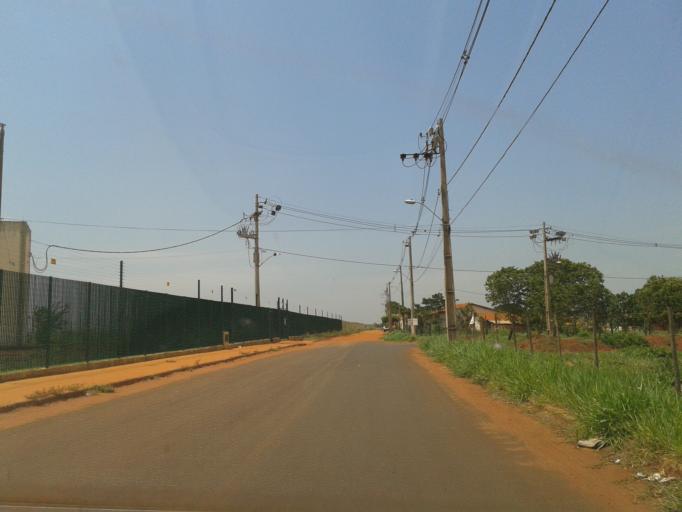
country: BR
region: Minas Gerais
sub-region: Ituiutaba
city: Ituiutaba
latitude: -18.9892
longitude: -49.4334
